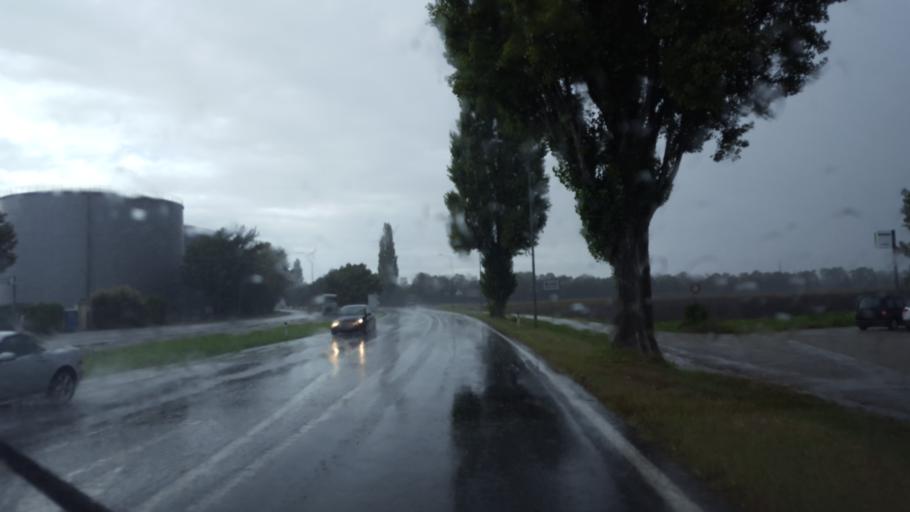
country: AT
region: Lower Austria
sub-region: Politischer Bezirk Bruck an der Leitha
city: Bruck an der Leitha
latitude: 48.0232
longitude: 16.7574
